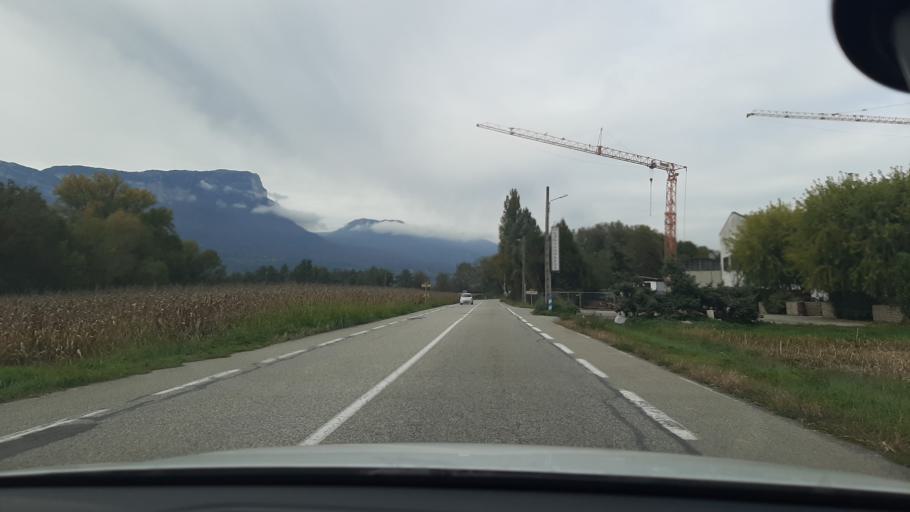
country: FR
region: Rhone-Alpes
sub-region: Departement de la Savoie
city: Montmelian
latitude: 45.4614
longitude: 6.0504
